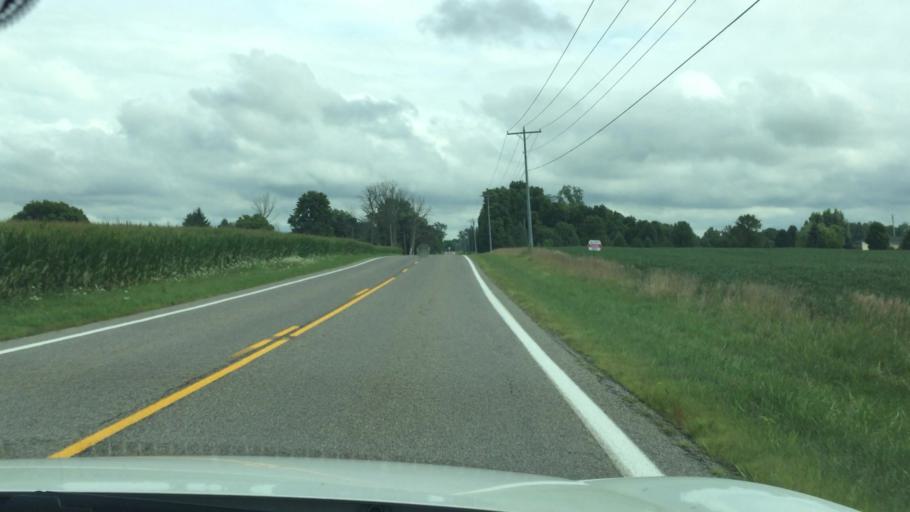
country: US
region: Ohio
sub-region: Champaign County
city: North Lewisburg
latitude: 40.2106
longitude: -83.5416
